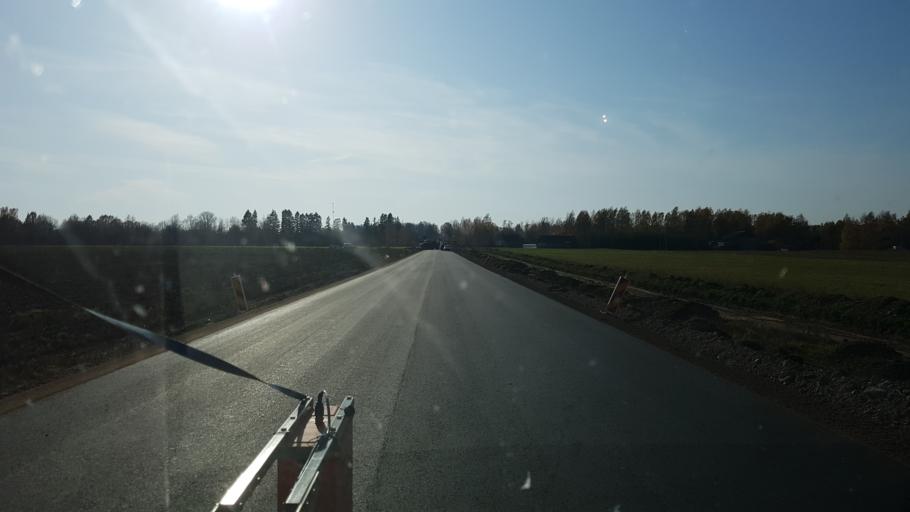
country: EE
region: Vorumaa
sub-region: Antsla vald
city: Vana-Antsla
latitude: 57.8373
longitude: 26.5451
